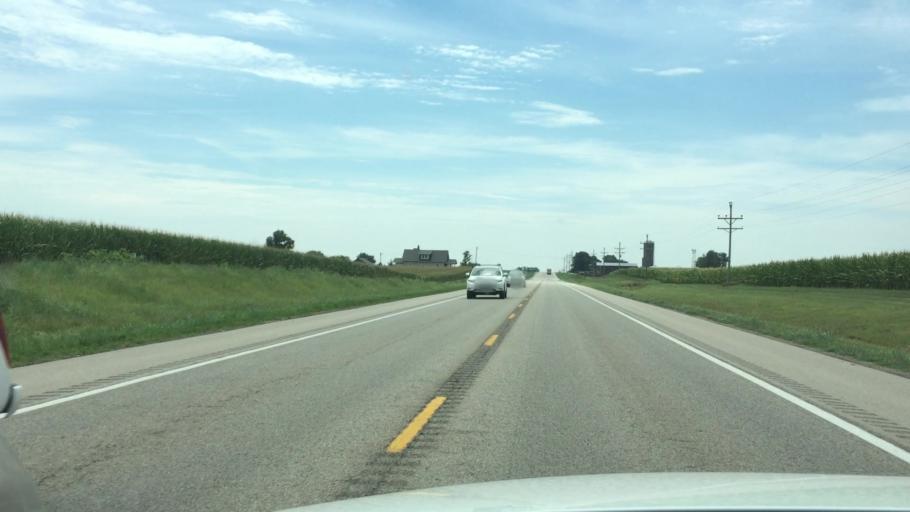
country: US
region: Kansas
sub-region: Nemaha County
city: Sabetha
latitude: 39.7792
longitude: -95.7295
